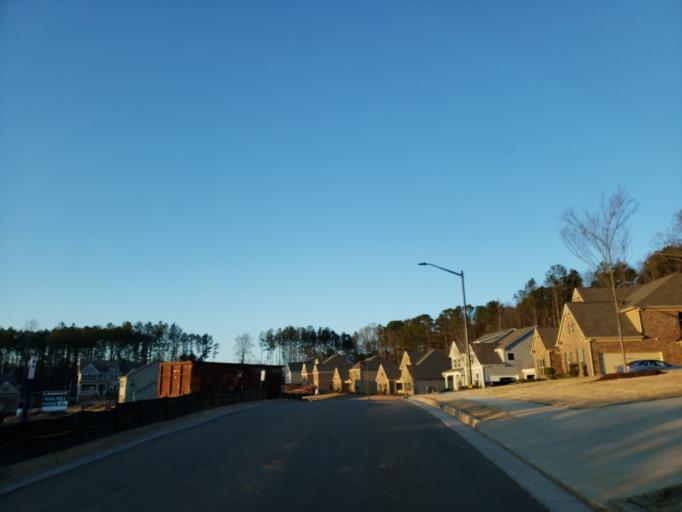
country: US
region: Georgia
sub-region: Cherokee County
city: Woodstock
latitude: 34.1183
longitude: -84.4500
